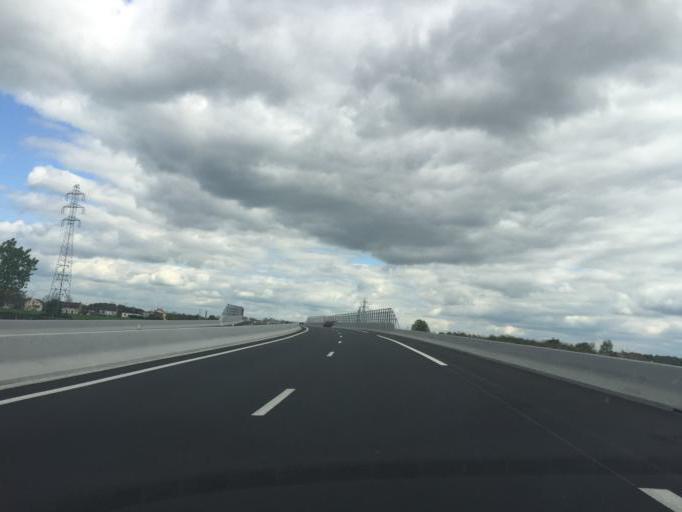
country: FR
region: Auvergne
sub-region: Departement de l'Allier
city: Varennes-sur-Allier
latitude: 46.3048
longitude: 3.4037
